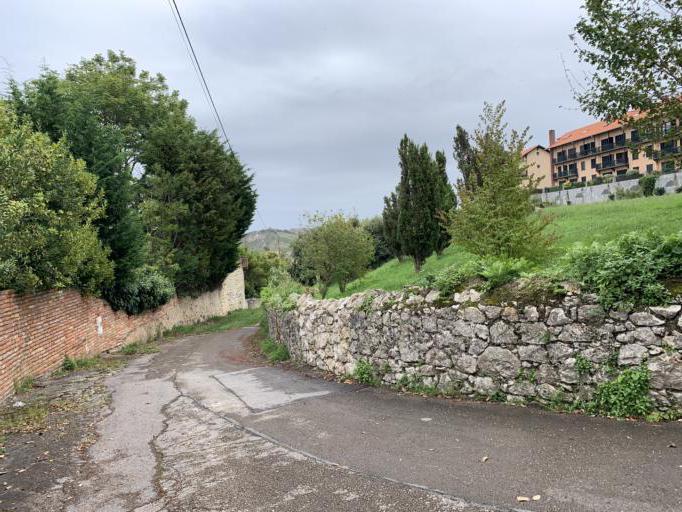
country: ES
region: Cantabria
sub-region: Provincia de Cantabria
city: Comillas
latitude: 43.3866
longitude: -4.2849
